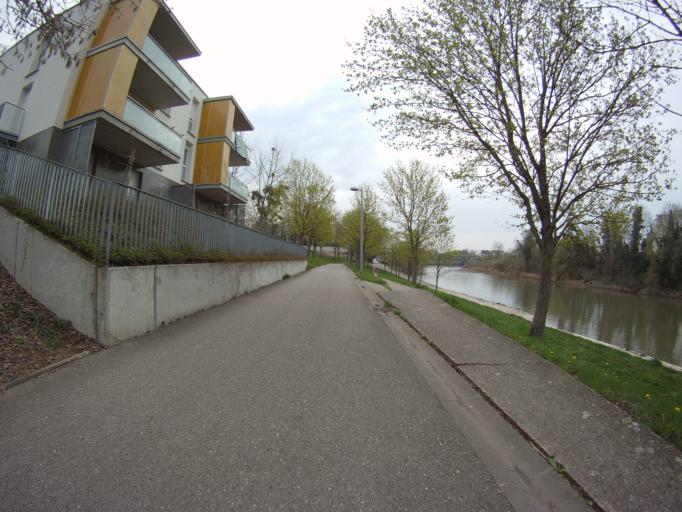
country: FR
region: Lorraine
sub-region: Departement de Meurthe-et-Moselle
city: Saint-Max
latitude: 48.7025
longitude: 6.1947
